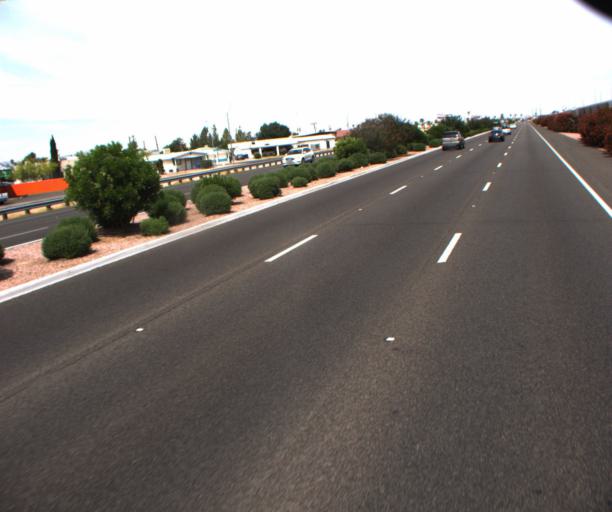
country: US
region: Arizona
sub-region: Maricopa County
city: El Mirage
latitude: 33.6134
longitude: -112.3177
